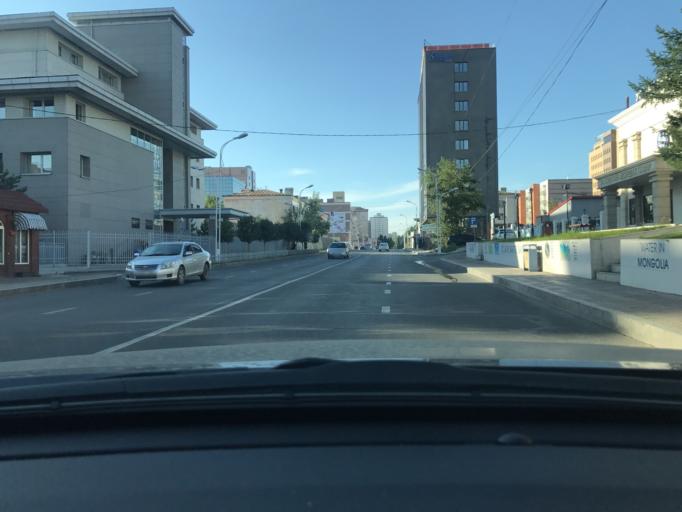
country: MN
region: Ulaanbaatar
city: Ulaanbaatar
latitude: 47.9195
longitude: 106.9352
